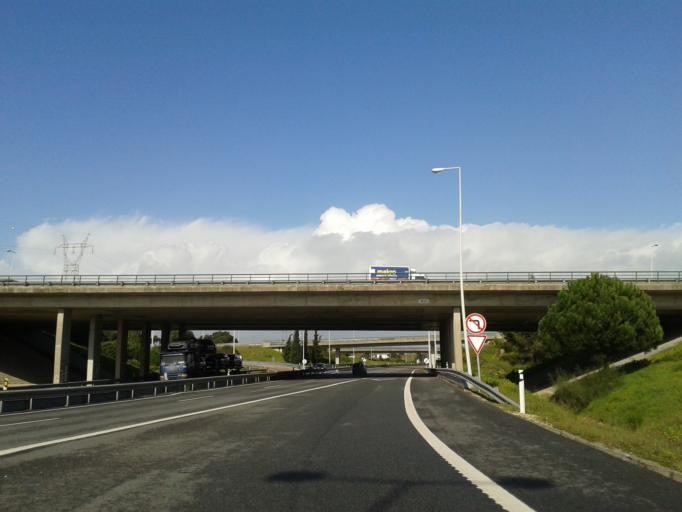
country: PT
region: Setubal
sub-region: Palmela
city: Palmela
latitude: 38.5806
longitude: -8.8630
